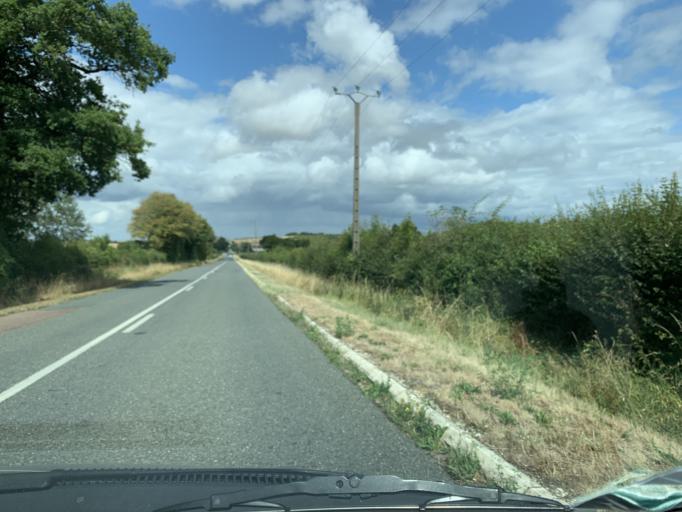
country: FR
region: Bourgogne
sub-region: Departement de la Nievre
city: Varzy
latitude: 47.3950
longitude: 3.4451
